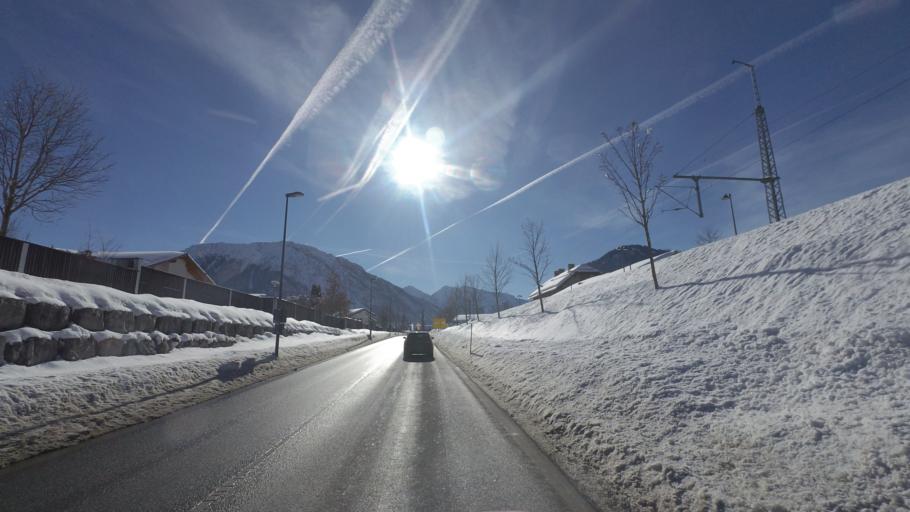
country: DE
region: Bavaria
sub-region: Upper Bavaria
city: Ruhpolding
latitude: 47.7630
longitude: 12.6489
